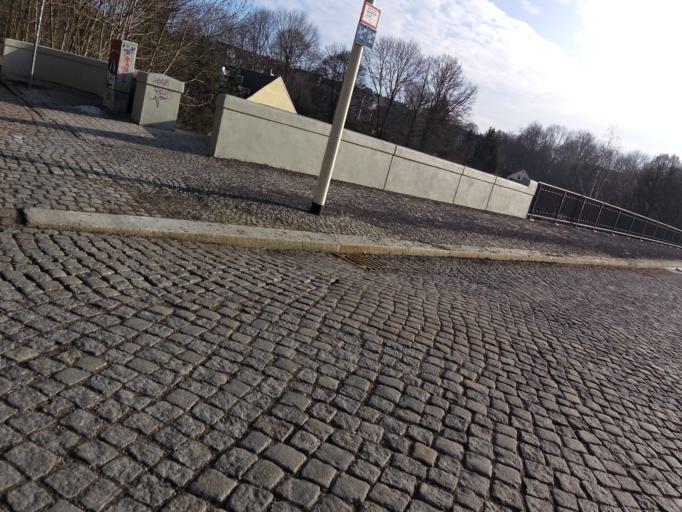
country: DE
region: Saxony
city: Glauchau
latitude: 50.8242
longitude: 12.5445
